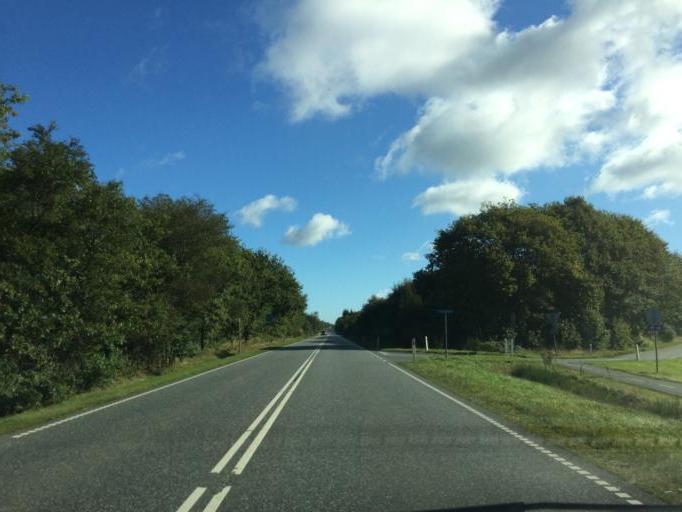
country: DK
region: Central Jutland
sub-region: Holstebro Kommune
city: Vinderup
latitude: 56.3924
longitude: 8.8258
